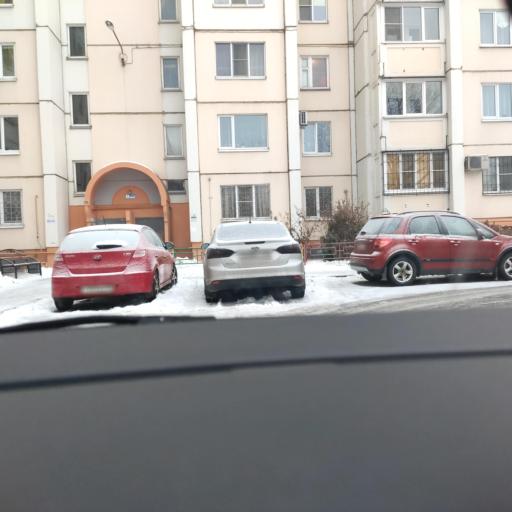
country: RU
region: Voronezj
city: Podgornoye
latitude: 51.7319
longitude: 39.2024
